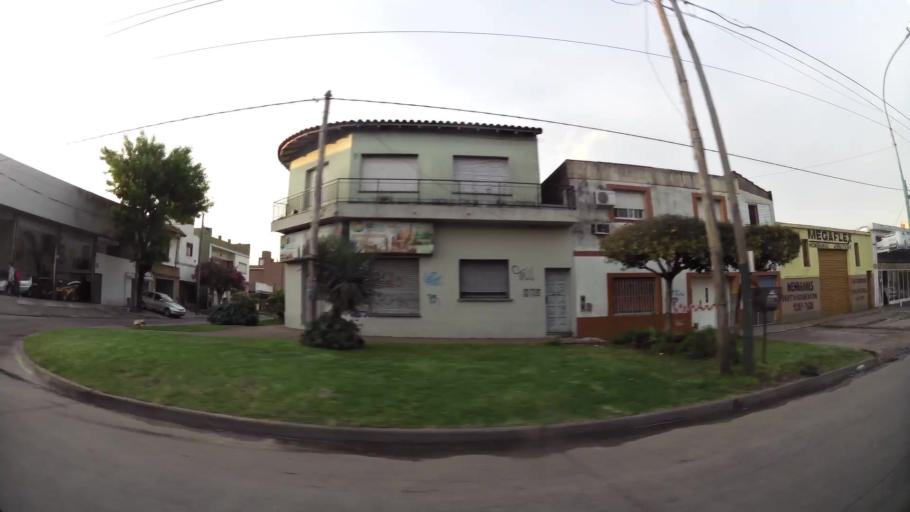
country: AR
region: Buenos Aires
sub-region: Partido de Lomas de Zamora
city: Lomas de Zamora
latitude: -34.7657
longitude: -58.3701
